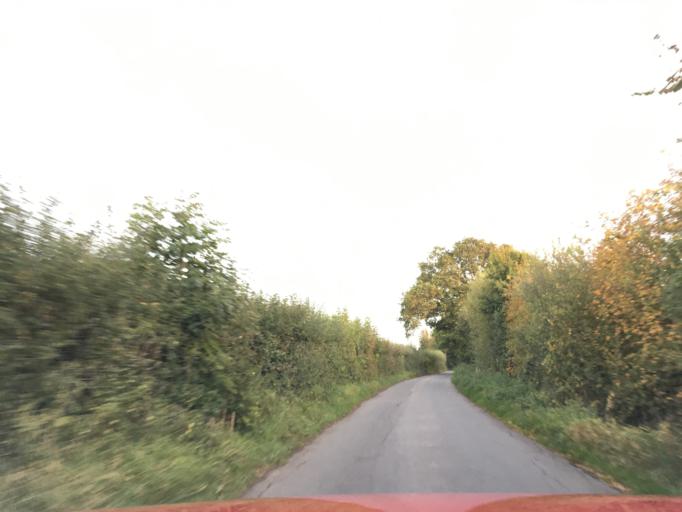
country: GB
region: England
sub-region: South Gloucestershire
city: Thornbury
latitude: 51.6246
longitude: -2.5529
